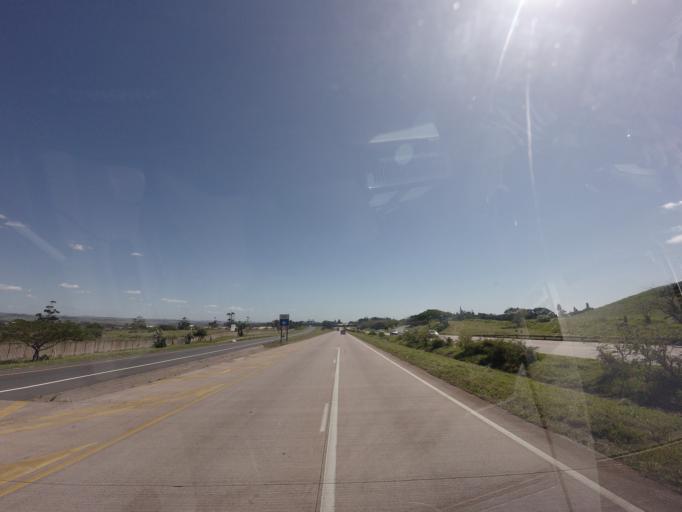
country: ZA
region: KwaZulu-Natal
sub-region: iLembe District Municipality
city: Ballitoville
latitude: -29.5053
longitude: 31.2082
